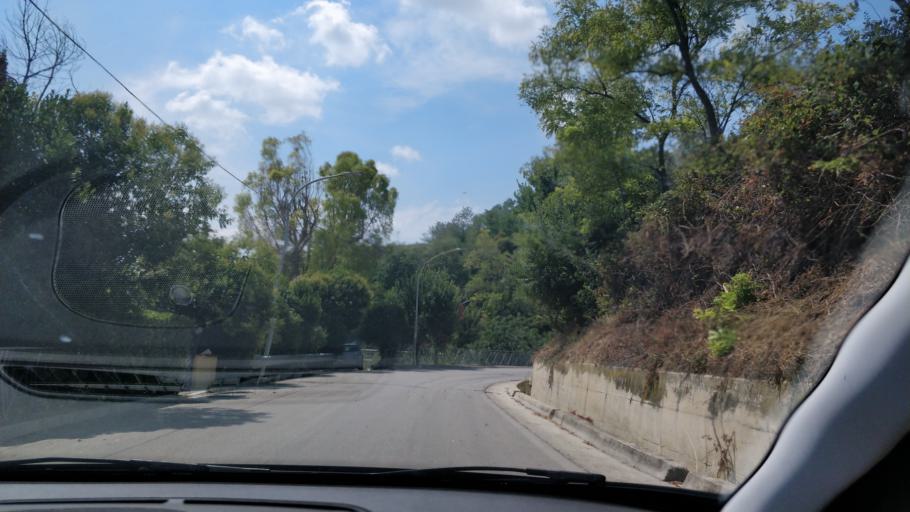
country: IT
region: Abruzzo
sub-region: Provincia di Chieti
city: Sambuceto
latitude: 42.4090
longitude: 14.2009
